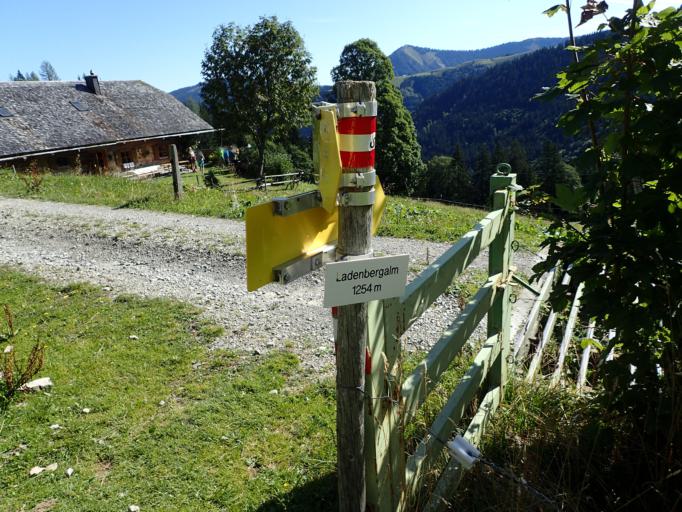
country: AT
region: Salzburg
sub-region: Politischer Bezirk Salzburg-Umgebung
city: Hintersee
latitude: 47.6965
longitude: 13.2584
